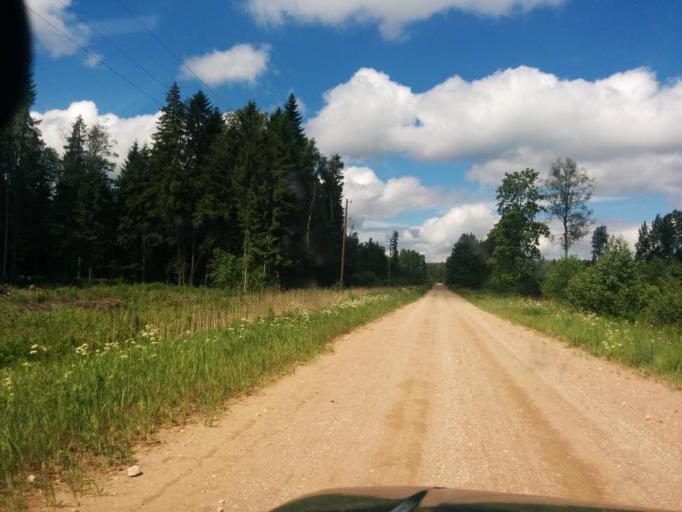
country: LV
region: Vilaka
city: Vilaka
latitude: 57.2677
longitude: 27.5736
